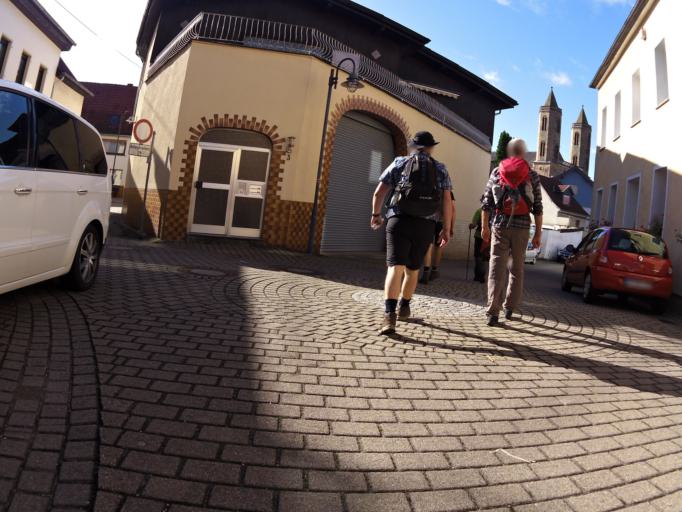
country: DE
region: Rheinland-Pfalz
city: Waldbockelheim
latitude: 49.8168
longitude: 7.7183
